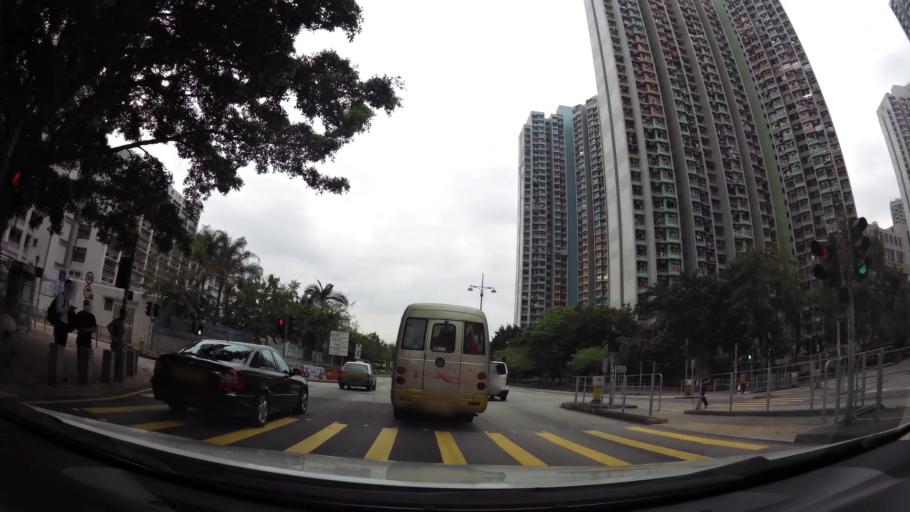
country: HK
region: Yuen Long
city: Yuen Long Kau Hui
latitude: 22.4527
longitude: 114.0027
